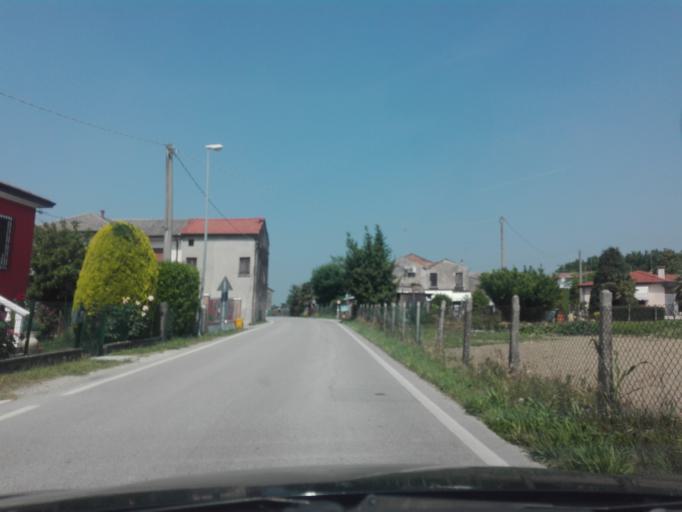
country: IT
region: Veneto
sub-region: Provincia di Rovigo
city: Adria
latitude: 45.0612
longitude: 11.9927
